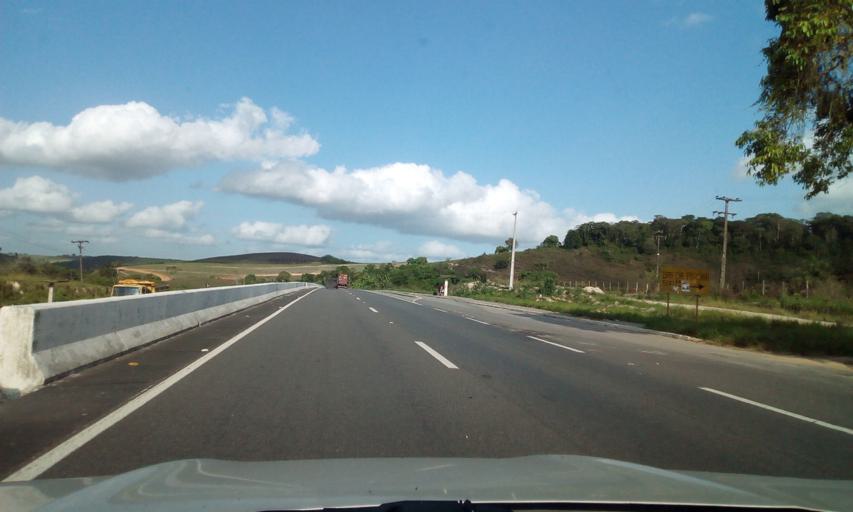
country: BR
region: Pernambuco
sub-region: Ribeirao
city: Ribeirao
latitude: -8.4466
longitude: -35.3435
